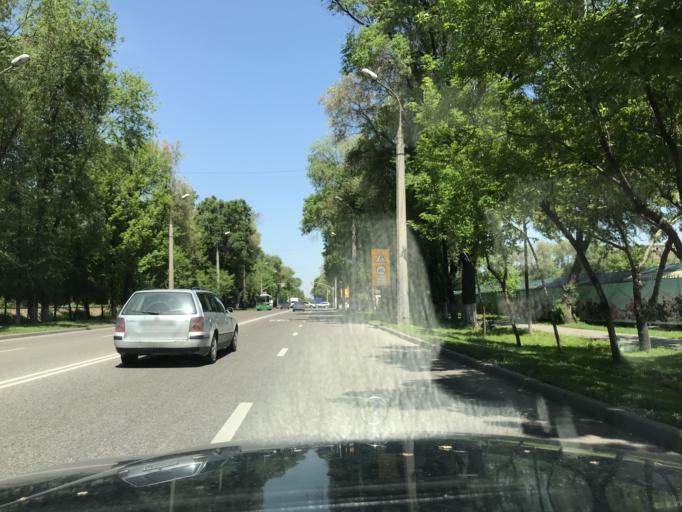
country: KZ
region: Almaty Oblysy
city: Pervomayskiy
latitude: 43.3248
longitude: 76.9592
